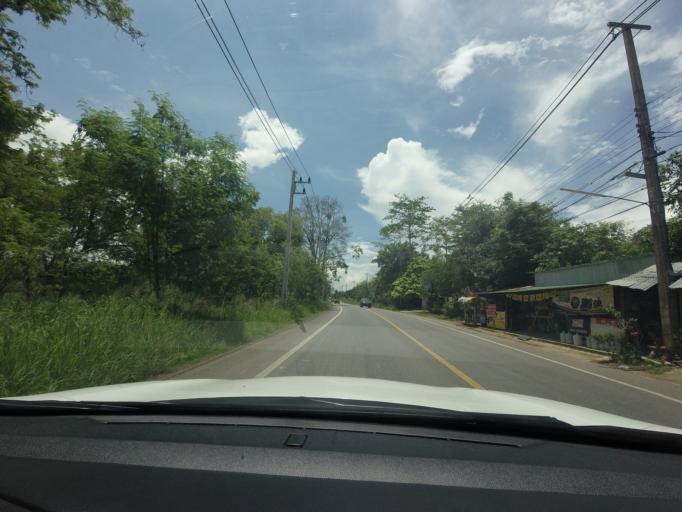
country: TH
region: Sara Buri
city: Muak Lek
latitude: 14.5978
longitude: 101.2154
